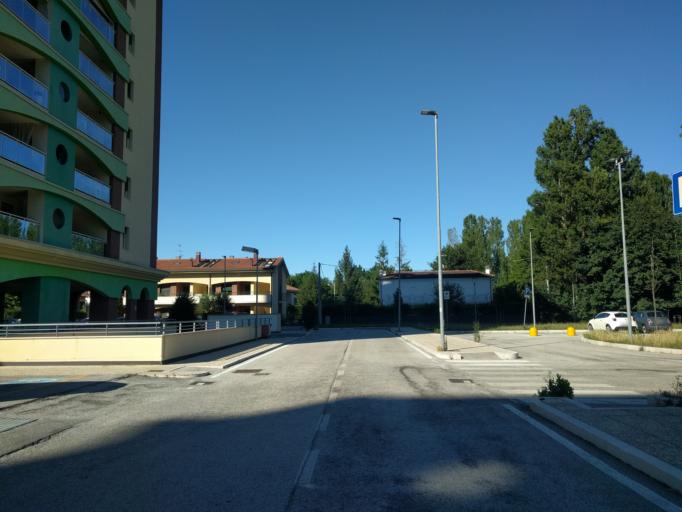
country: IT
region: The Marches
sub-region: Provincia di Pesaro e Urbino
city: Pesaro
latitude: 43.8886
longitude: 12.9098
